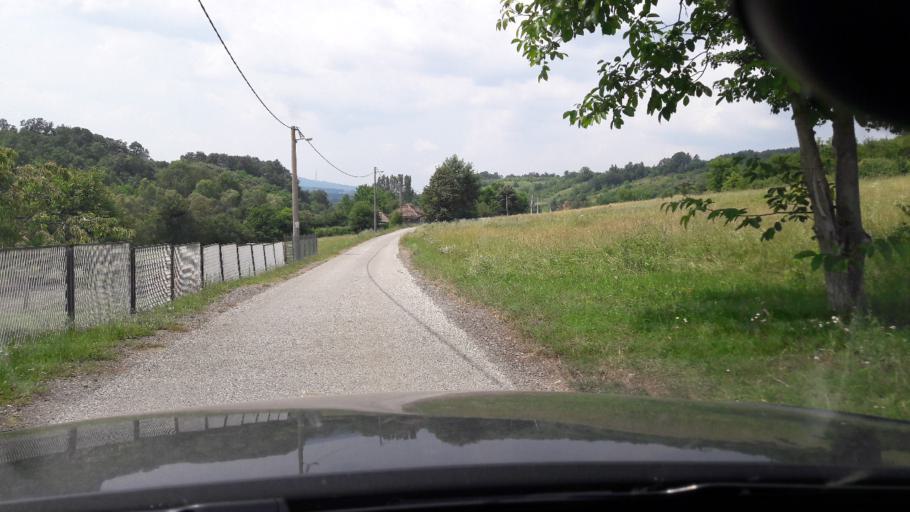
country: RS
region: Central Serbia
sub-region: Belgrade
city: Sopot
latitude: 44.6301
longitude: 20.5948
